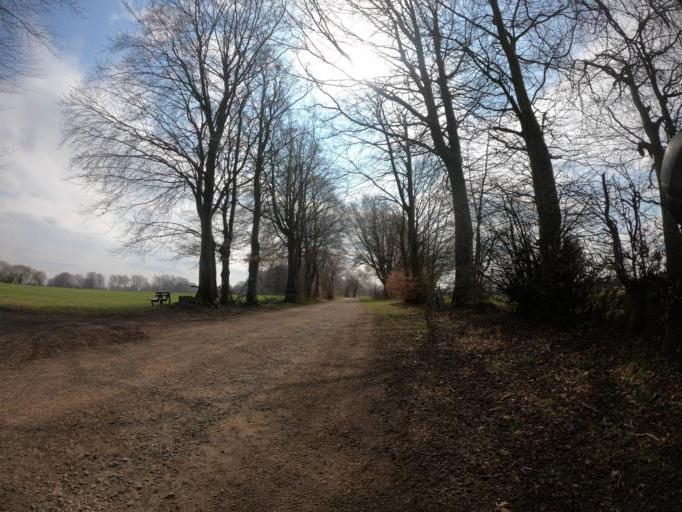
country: DE
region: North Rhine-Westphalia
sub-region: Regierungsbezirk Koln
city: Simmerath
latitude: 50.6051
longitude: 6.2832
